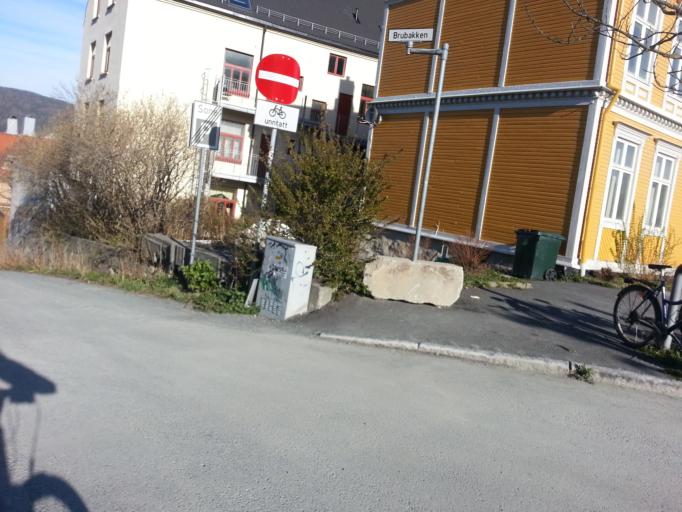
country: NO
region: Sor-Trondelag
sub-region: Trondheim
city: Trondheim
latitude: 63.4280
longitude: 10.4060
